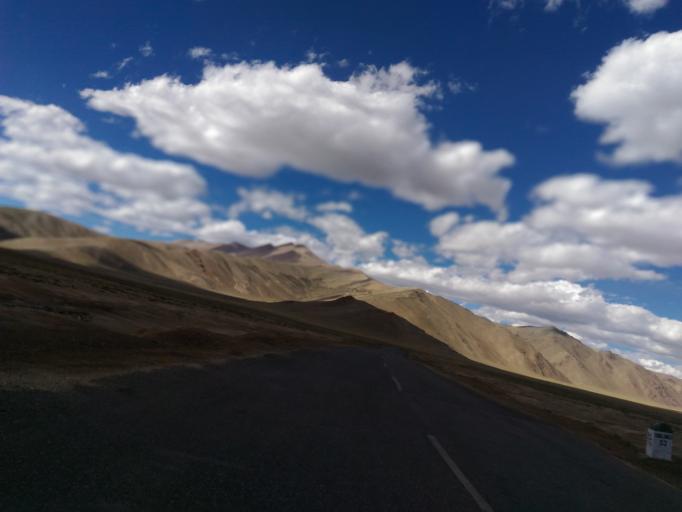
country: IN
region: Kashmir
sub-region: Kargil
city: Padam
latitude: 33.2084
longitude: 77.7961
